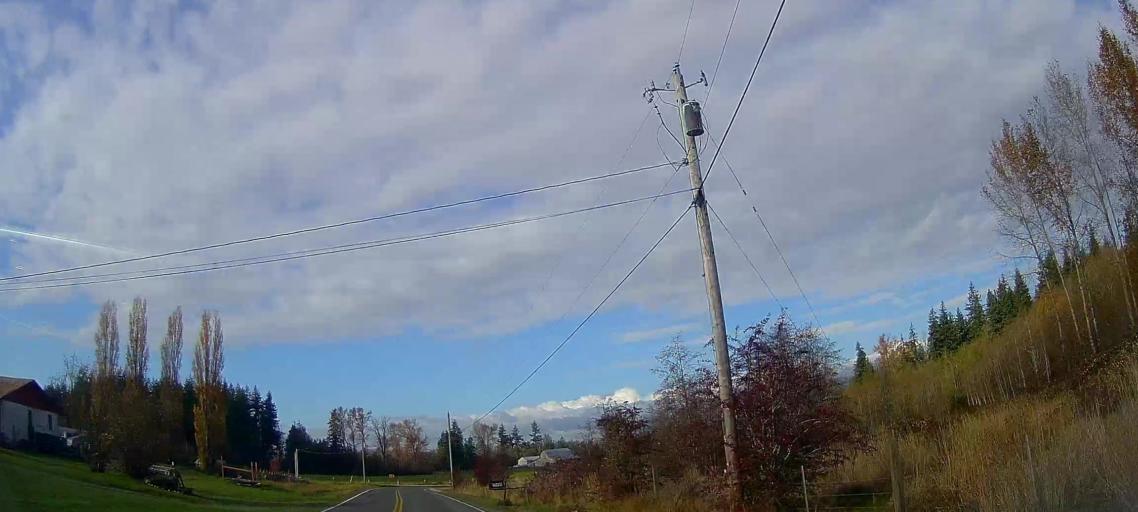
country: US
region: Washington
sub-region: Skagit County
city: Big Lake
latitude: 48.4275
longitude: -122.2407
